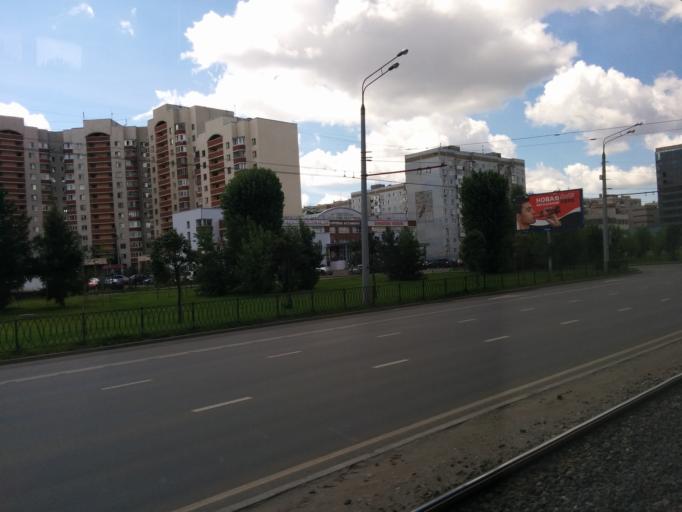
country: RU
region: Tatarstan
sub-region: Gorod Kazan'
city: Kazan
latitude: 55.8270
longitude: 49.1246
